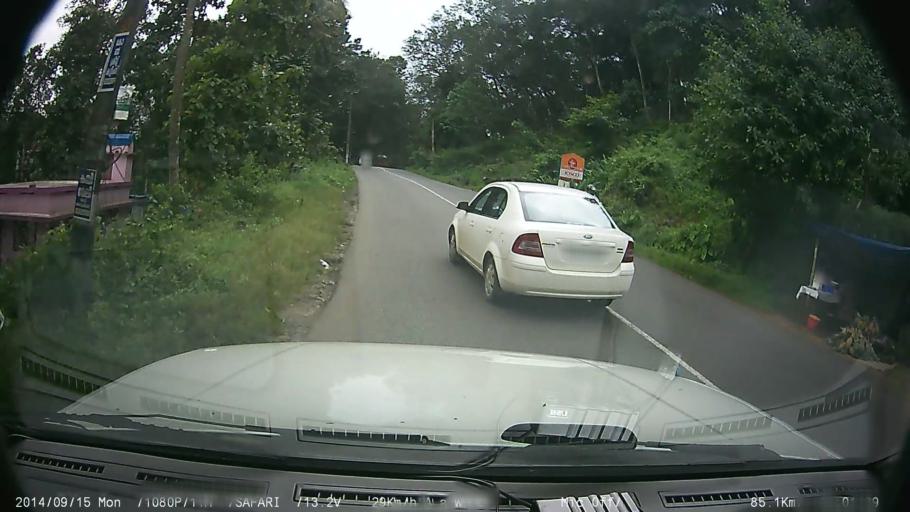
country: IN
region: Kerala
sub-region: Ernakulam
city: Muvattupuzha
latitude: 9.9320
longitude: 76.5752
